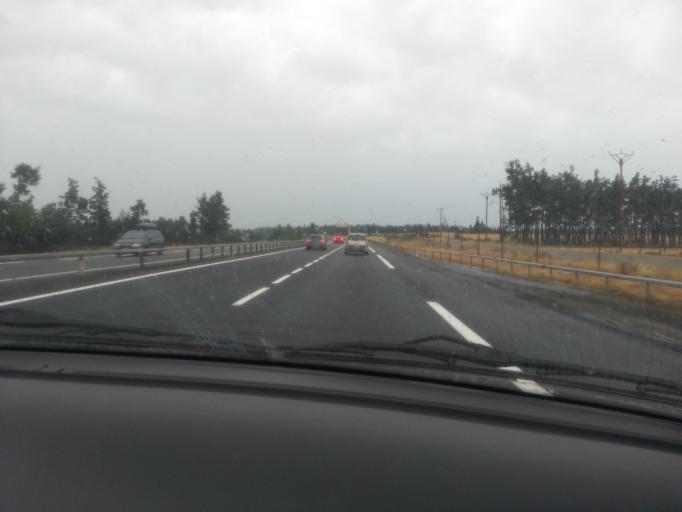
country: FR
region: Languedoc-Roussillon
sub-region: Departement de la Lozere
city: Aumont-Aubrac
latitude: 44.6960
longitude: 3.2816
